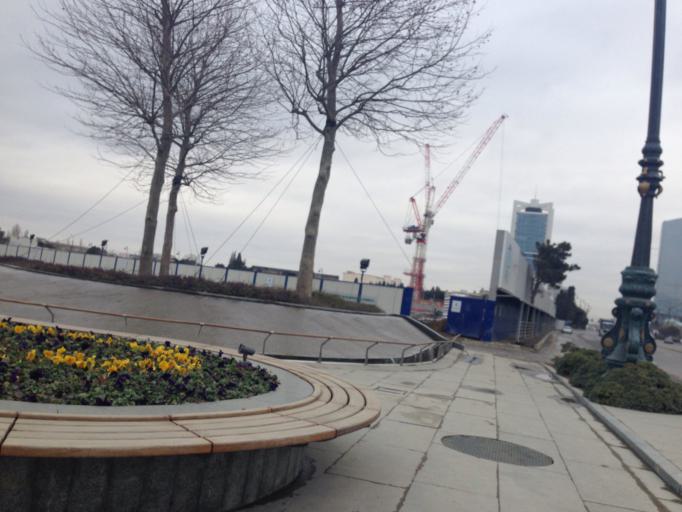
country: AZ
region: Baki
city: Baku
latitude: 40.4115
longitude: 49.8960
